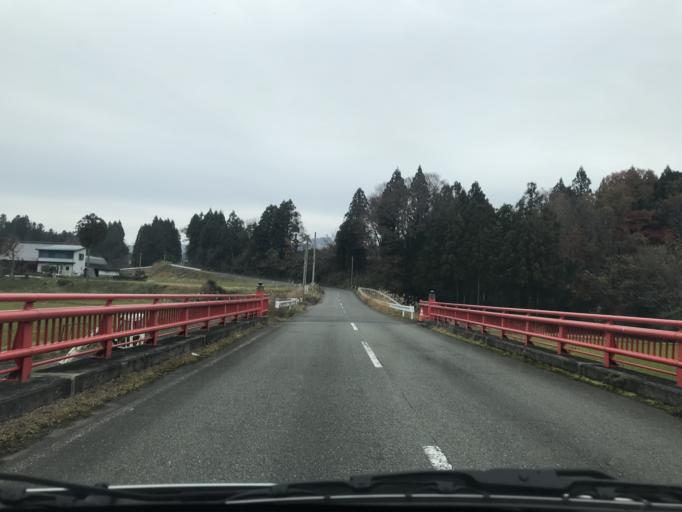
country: JP
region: Iwate
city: Mizusawa
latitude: 39.0280
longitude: 141.0730
